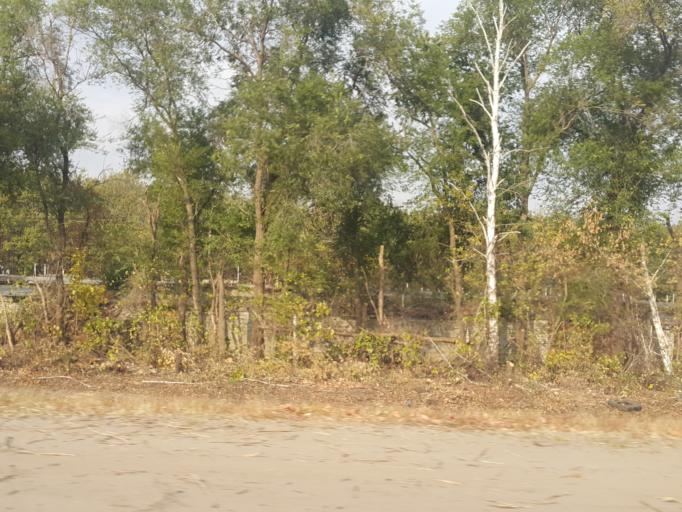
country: RU
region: Tambov
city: Bokino
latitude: 52.6680
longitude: 41.4519
